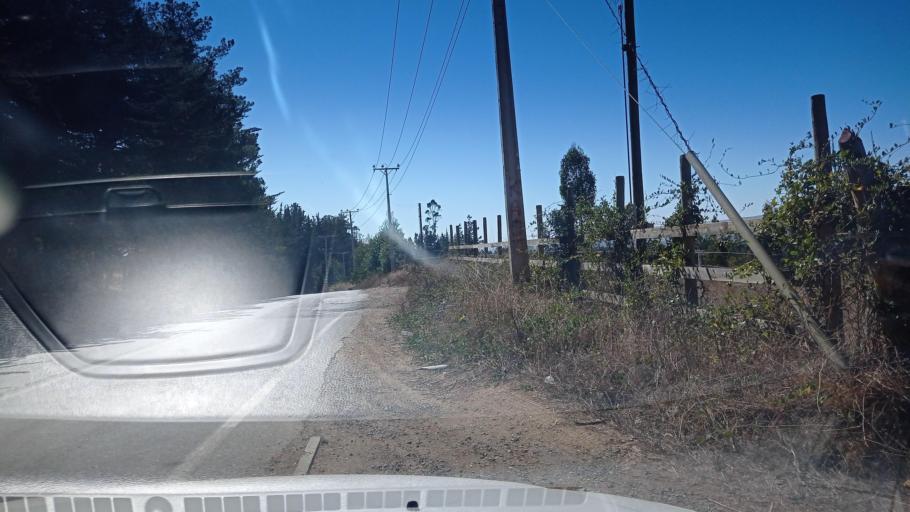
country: CL
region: O'Higgins
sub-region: Provincia de Colchagua
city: Santa Cruz
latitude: -34.4202
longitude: -72.0010
